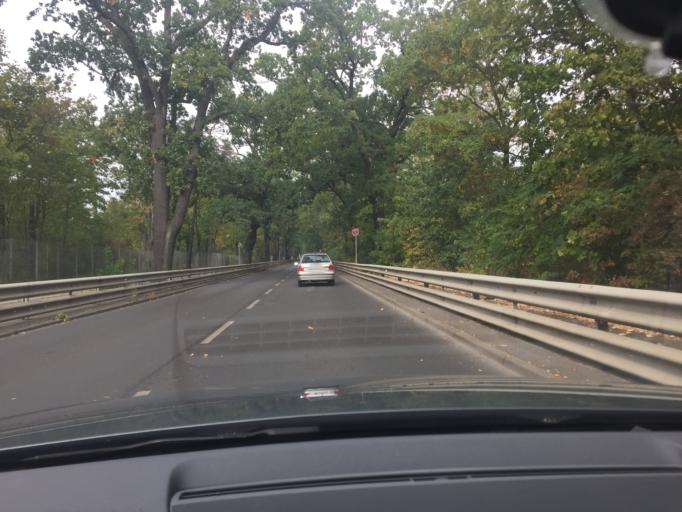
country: DE
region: Berlin
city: Rahnsdorf
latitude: 52.4457
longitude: 13.6763
